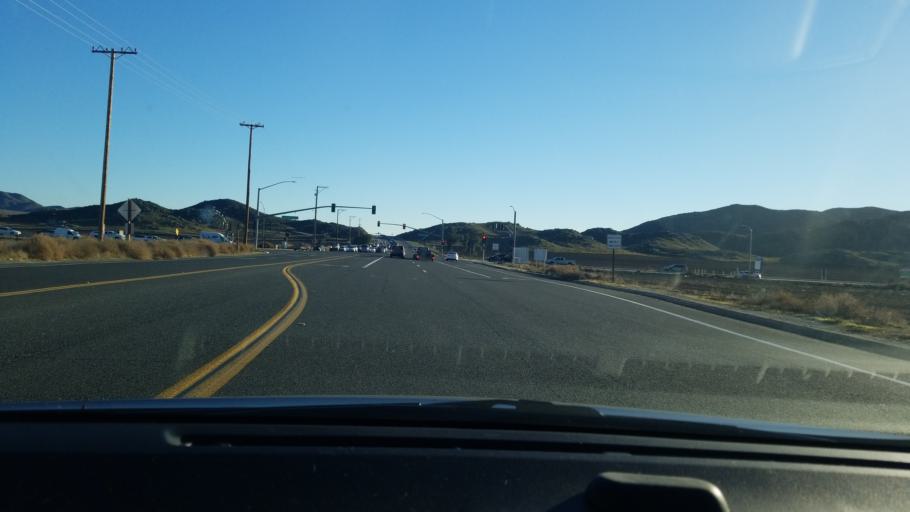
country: US
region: California
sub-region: Riverside County
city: Winchester
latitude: 33.6975
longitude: -117.0849
